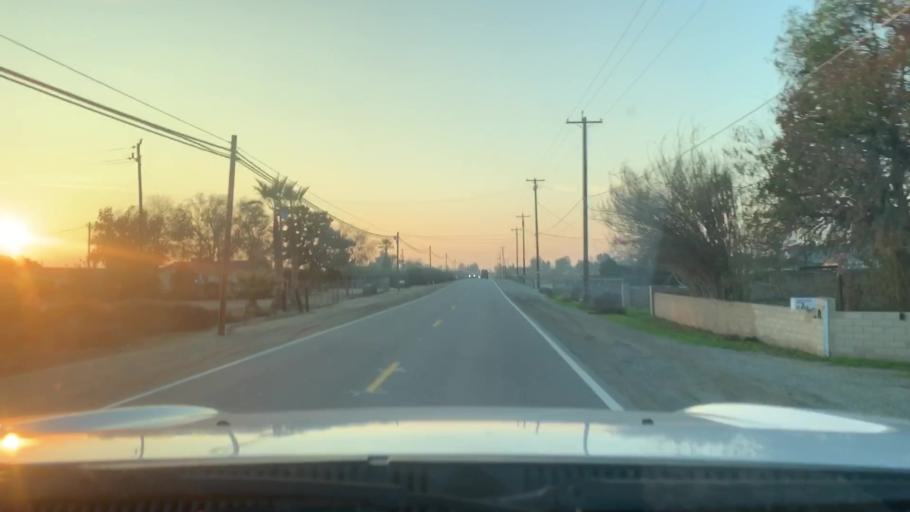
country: US
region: California
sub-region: Kern County
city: Rosedale
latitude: 35.3835
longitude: -119.1932
